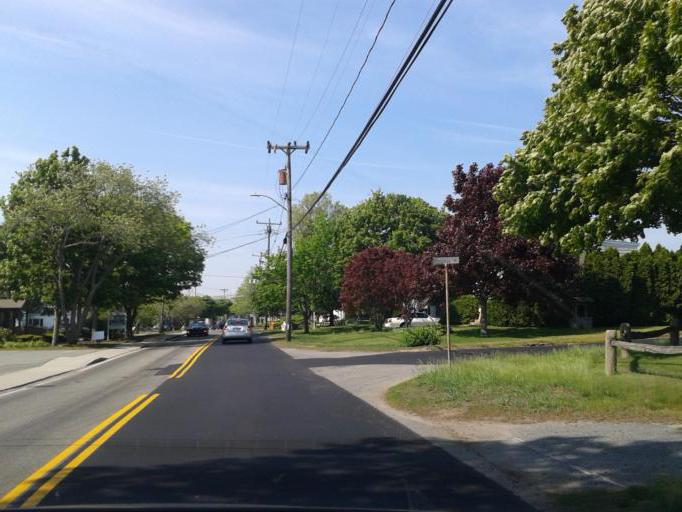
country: US
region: Massachusetts
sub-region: Barnstable County
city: Teaticket
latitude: 41.5536
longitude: -70.6000
